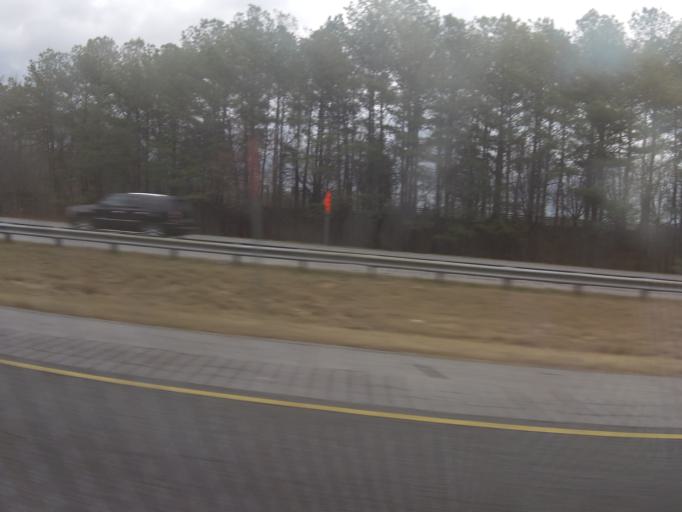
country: US
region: Georgia
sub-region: Gordon County
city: Calhoun
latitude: 34.6347
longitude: -84.9768
